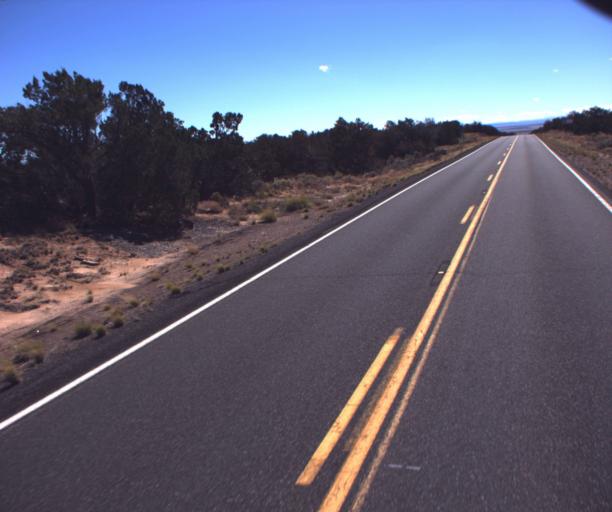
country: US
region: Arizona
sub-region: Apache County
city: Saint Johns
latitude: 34.8372
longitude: -109.2375
